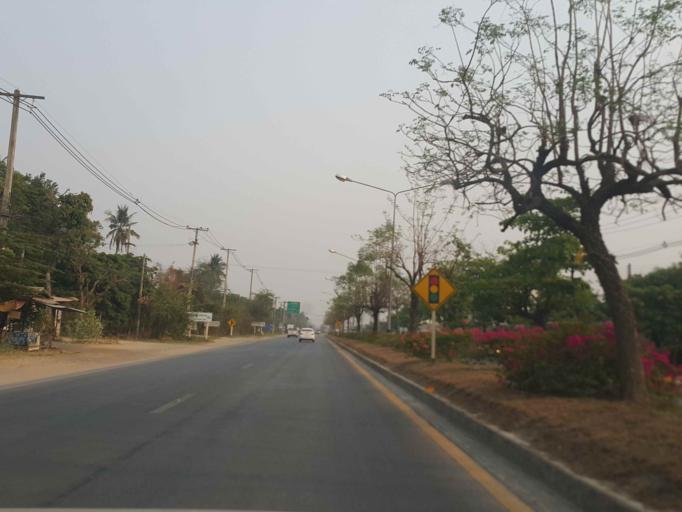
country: TH
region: Chiang Mai
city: San Sai
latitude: 18.9245
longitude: 98.9930
